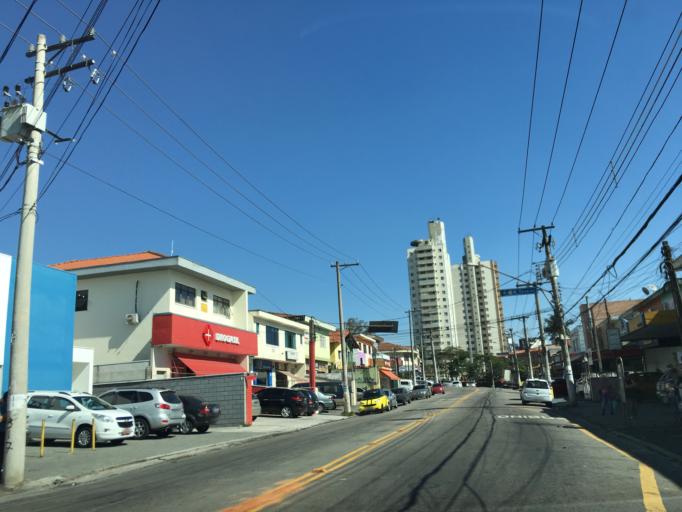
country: BR
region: Sao Paulo
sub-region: Taboao Da Serra
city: Taboao da Serra
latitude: -23.5822
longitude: -46.7602
